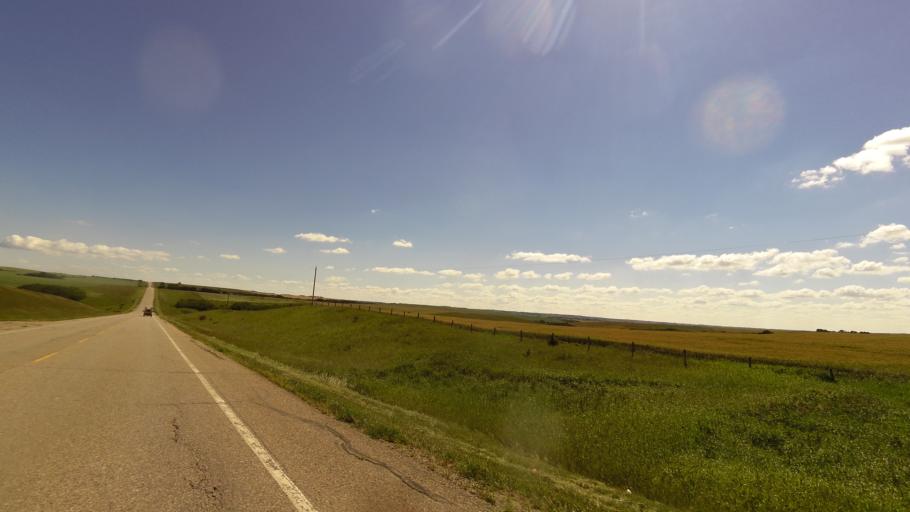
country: CA
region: Saskatchewan
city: Lloydminster
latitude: 52.8419
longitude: -110.0380
